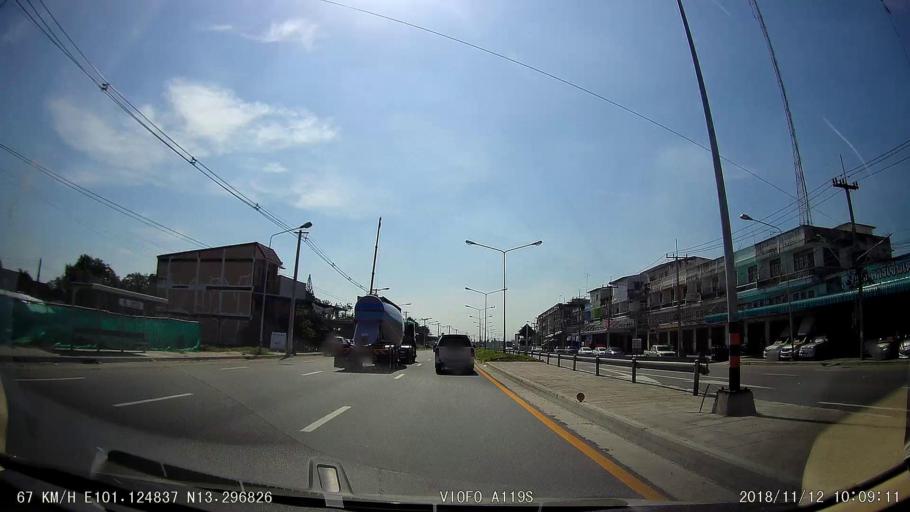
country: TH
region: Chon Buri
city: Ban Bueng
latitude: 13.2966
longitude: 101.1250
